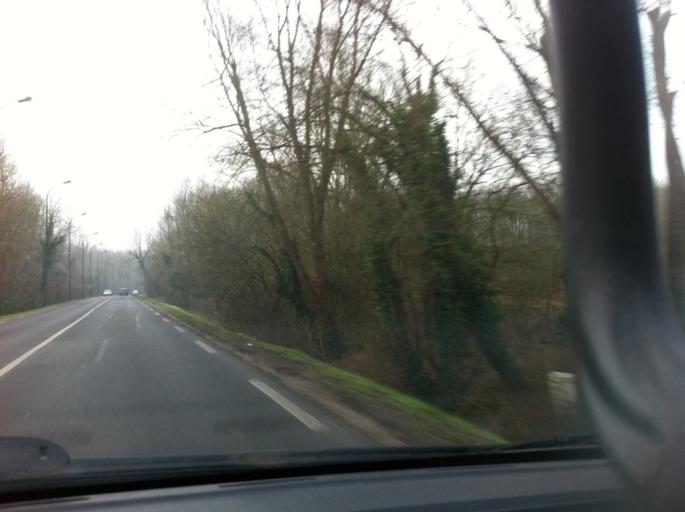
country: FR
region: Ile-de-France
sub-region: Departement de l'Essonne
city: Etampes
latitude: 48.4244
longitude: 2.1536
